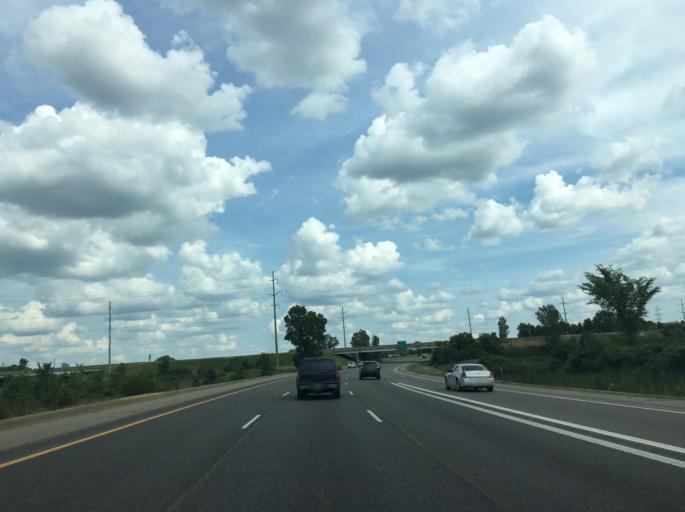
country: US
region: Michigan
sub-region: Genesee County
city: Grand Blanc
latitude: 42.9072
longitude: -83.6532
